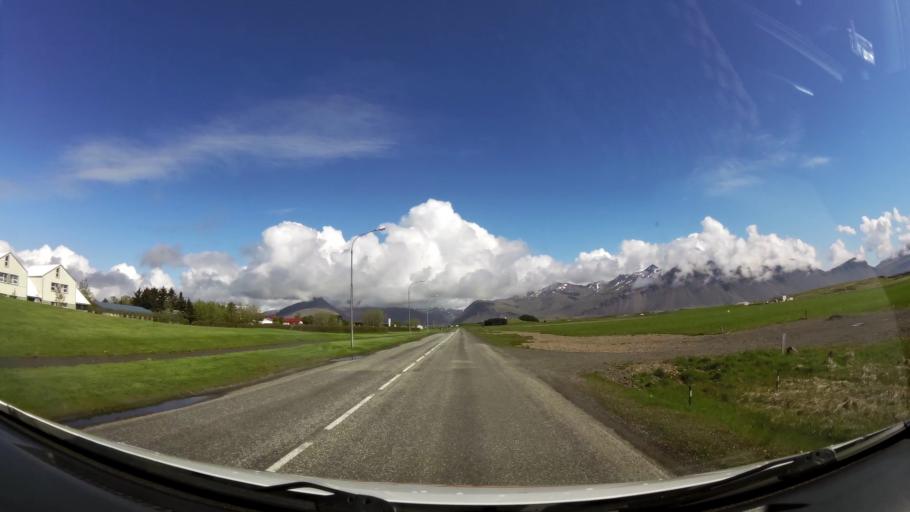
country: IS
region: East
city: Hoefn
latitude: 64.2604
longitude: -15.2037
